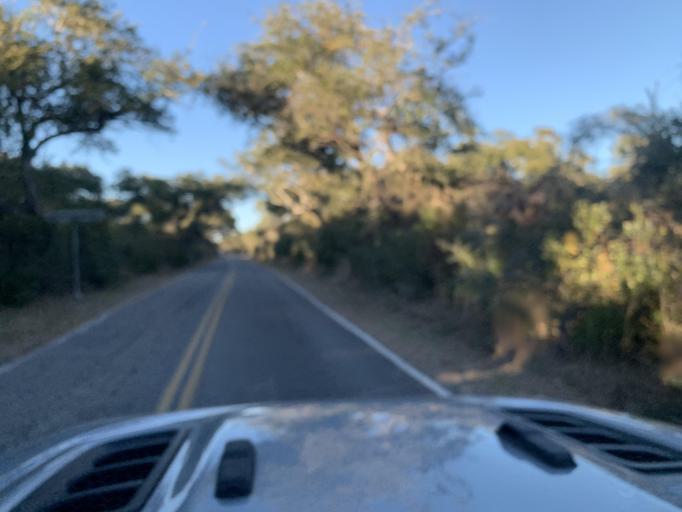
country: US
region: Texas
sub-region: Aransas County
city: Fulton
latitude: 28.1478
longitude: -96.9843
